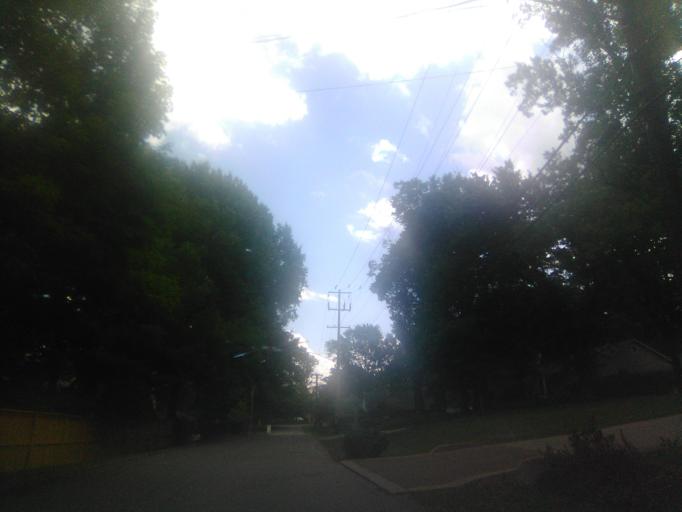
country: US
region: Tennessee
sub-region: Davidson County
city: Belle Meade
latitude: 36.1101
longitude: -86.8284
